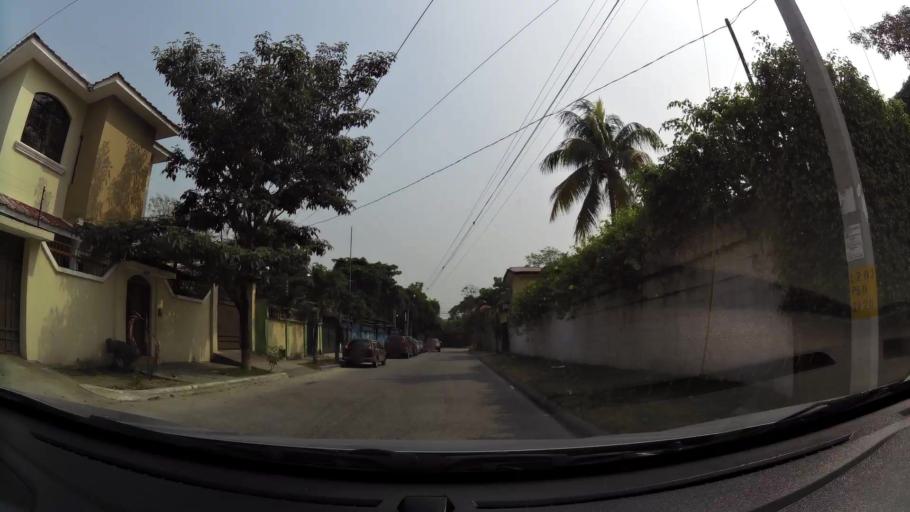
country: HN
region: Cortes
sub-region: San Pedro Sula
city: Pena Blanca
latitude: 15.5253
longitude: -88.0313
